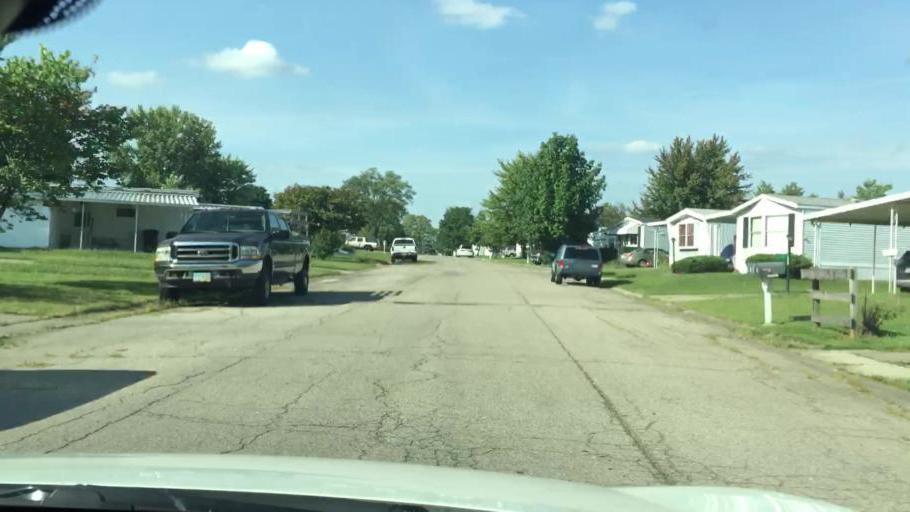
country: US
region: Ohio
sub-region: Clark County
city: Northridge
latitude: 39.9511
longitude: -83.6848
